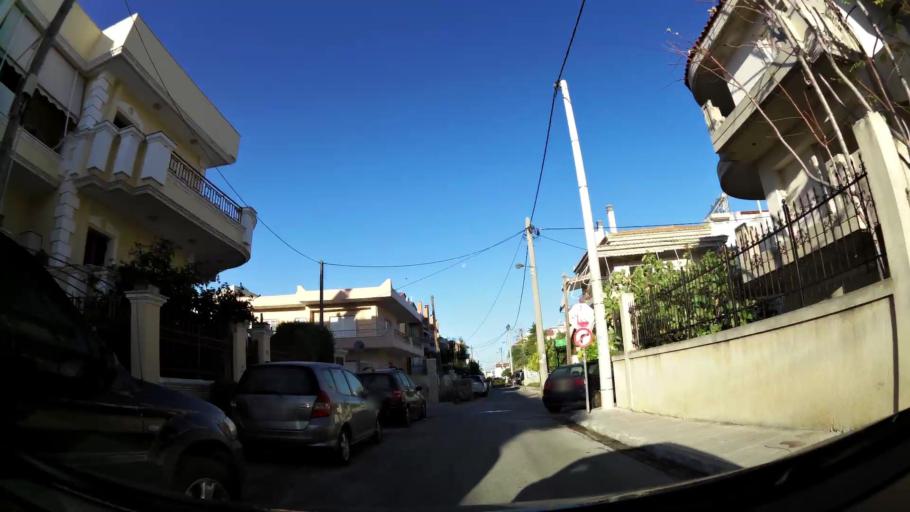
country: GR
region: Attica
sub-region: Nomarchia Anatolikis Attikis
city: Gerakas
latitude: 38.0249
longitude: 23.8453
